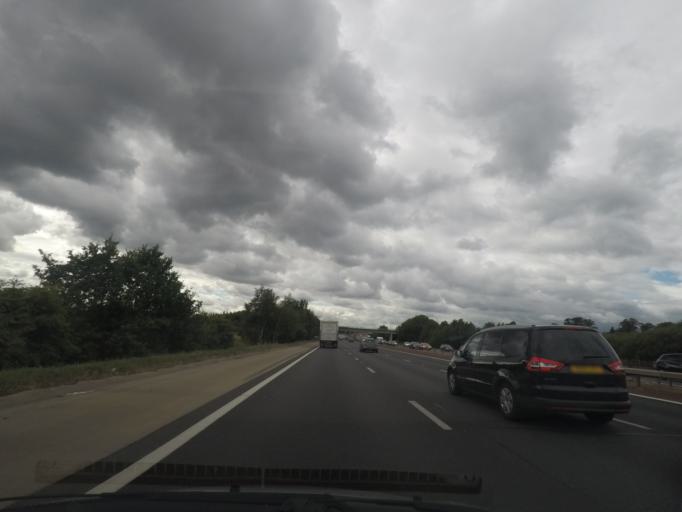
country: GB
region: England
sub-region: City and Borough of Leeds
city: Garforth
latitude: 53.8042
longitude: -1.3856
